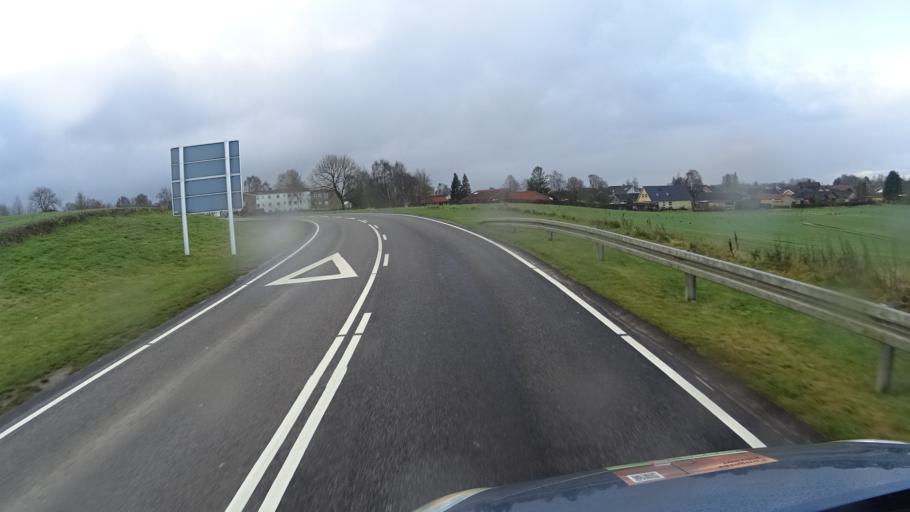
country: DK
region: South Denmark
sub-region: Vejle Kommune
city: Jelling
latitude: 55.7589
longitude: 9.4147
